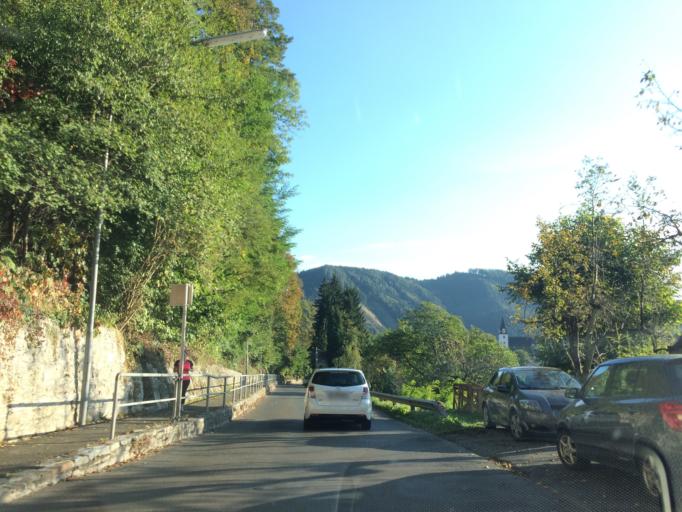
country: AT
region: Styria
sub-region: Politischer Bezirk Leoben
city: Leoben
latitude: 47.3685
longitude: 15.0981
